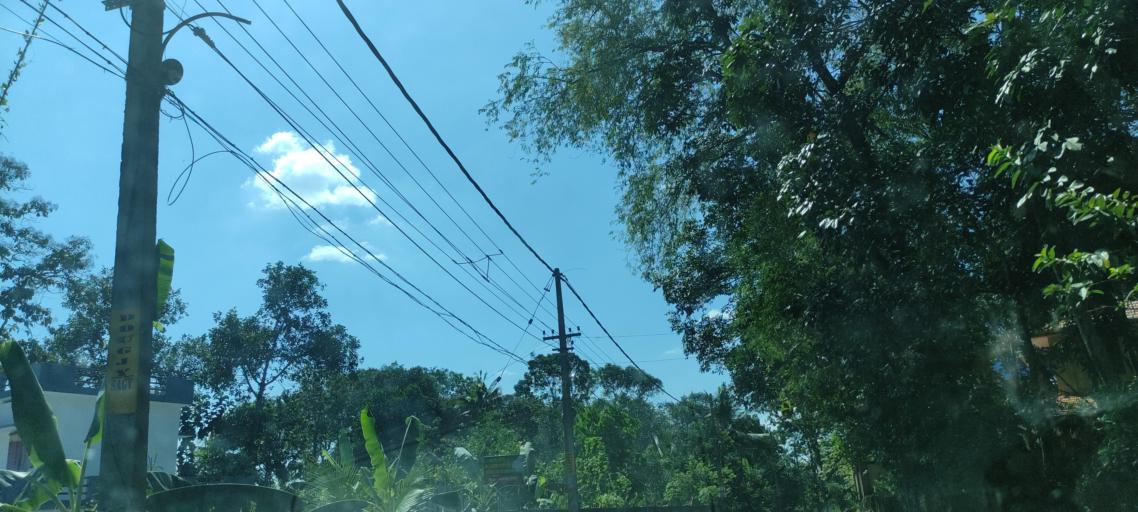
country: IN
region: Kerala
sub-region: Pattanamtitta
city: Adur
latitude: 9.0951
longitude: 76.7332
